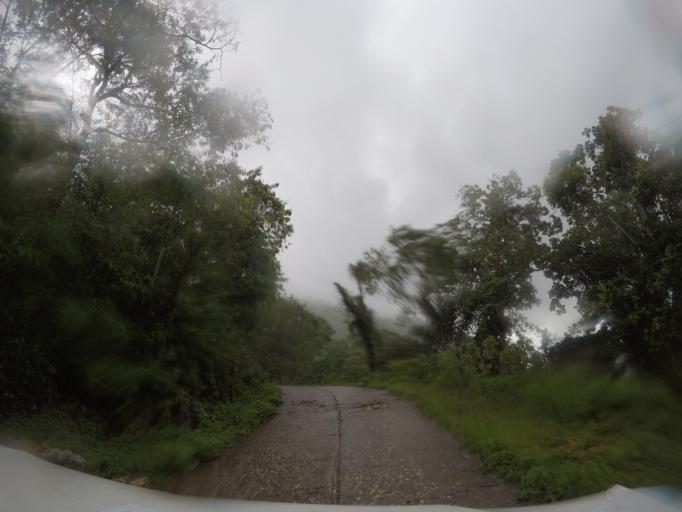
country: TL
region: Baucau
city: Venilale
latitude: -8.6292
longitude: 126.4395
